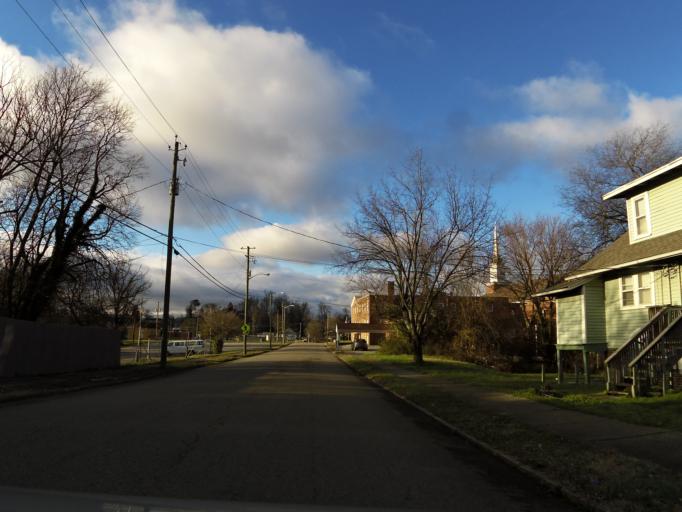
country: US
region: Tennessee
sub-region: Knox County
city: Knoxville
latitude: 35.9965
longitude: -83.8765
